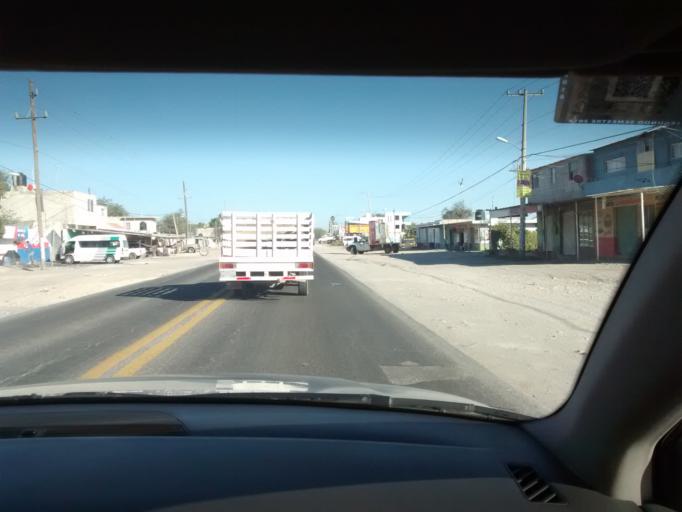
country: MX
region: Puebla
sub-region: Santiago Miahuatlan
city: San Jose Monte Chiquito
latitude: 18.4935
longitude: -97.4659
